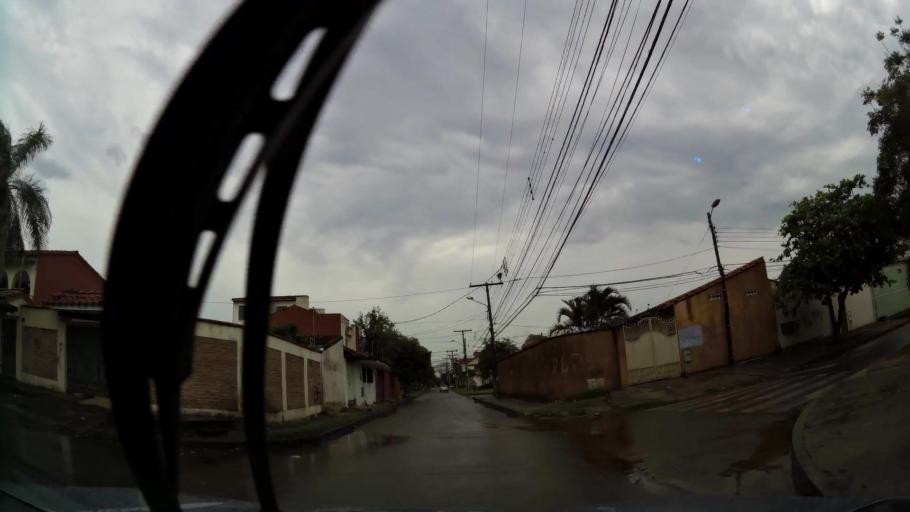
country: BO
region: Santa Cruz
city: Santa Cruz de la Sierra
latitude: -17.7661
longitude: -63.1533
